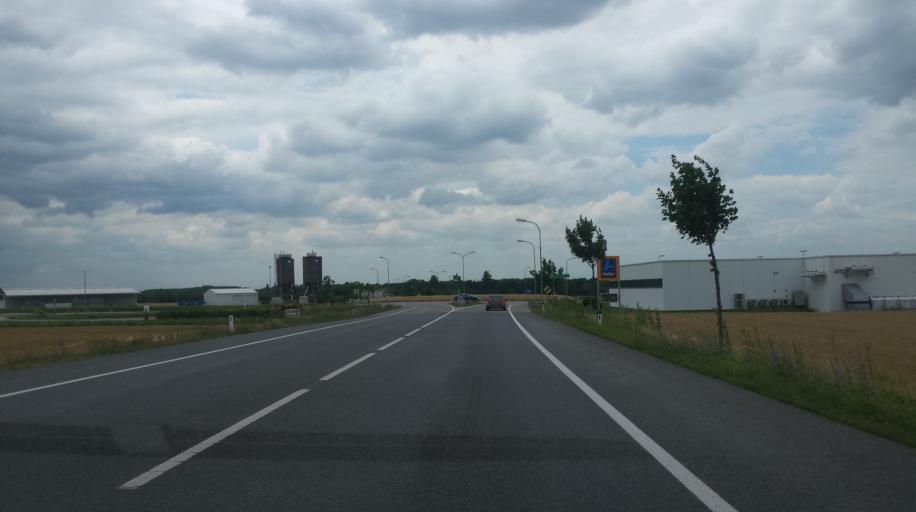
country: AT
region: Lower Austria
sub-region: Politischer Bezirk Wien-Umgebung
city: Himberg
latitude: 48.0726
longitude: 16.4599
